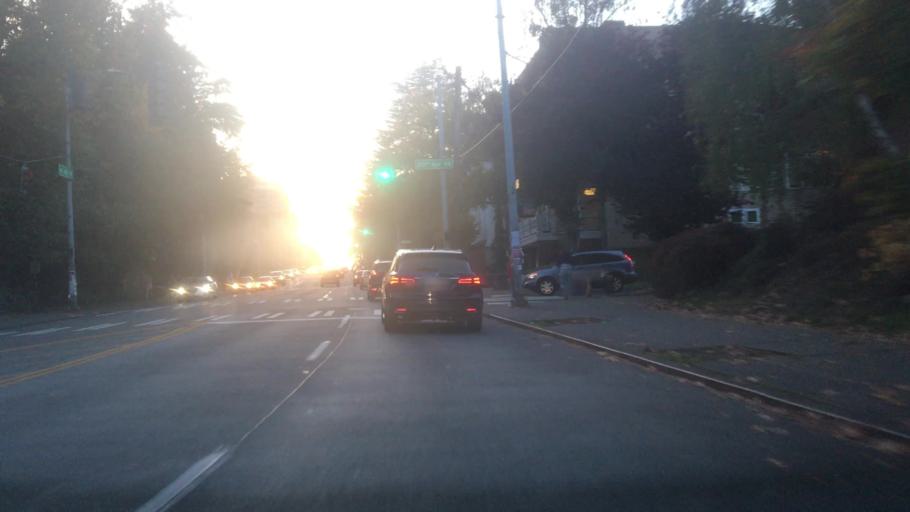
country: US
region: Washington
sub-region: King County
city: Seattle
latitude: 47.6613
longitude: -122.3061
